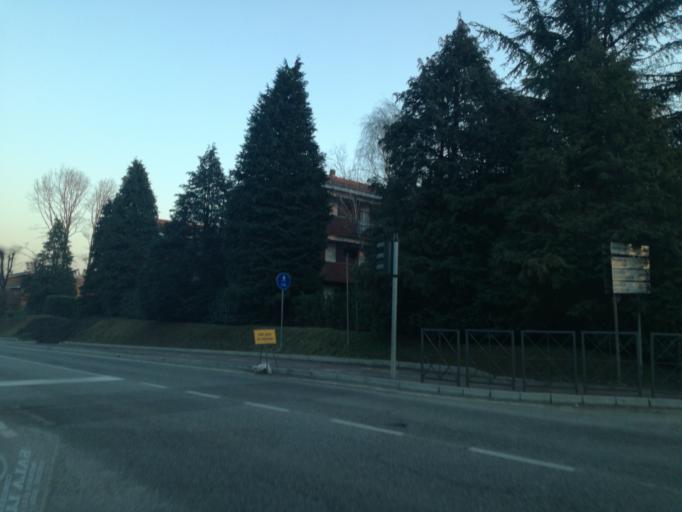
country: IT
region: Lombardy
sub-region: Provincia di Lecco
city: Quattro Strade
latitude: 45.6953
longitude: 9.3788
